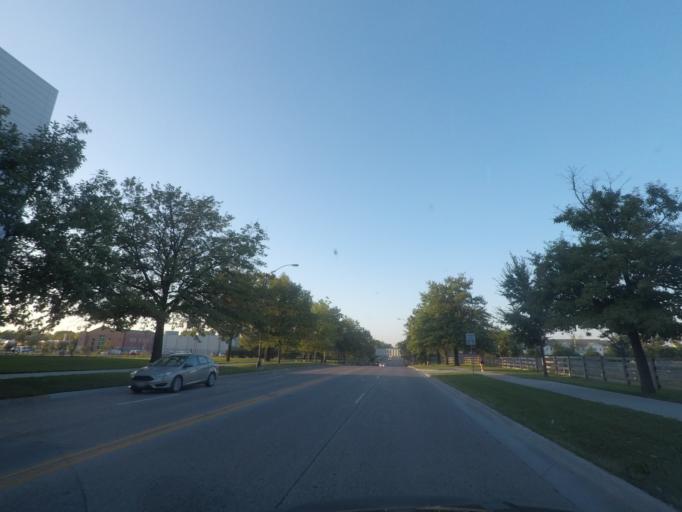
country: US
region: Iowa
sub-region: Story County
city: Ames
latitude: 42.0307
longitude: -93.6447
